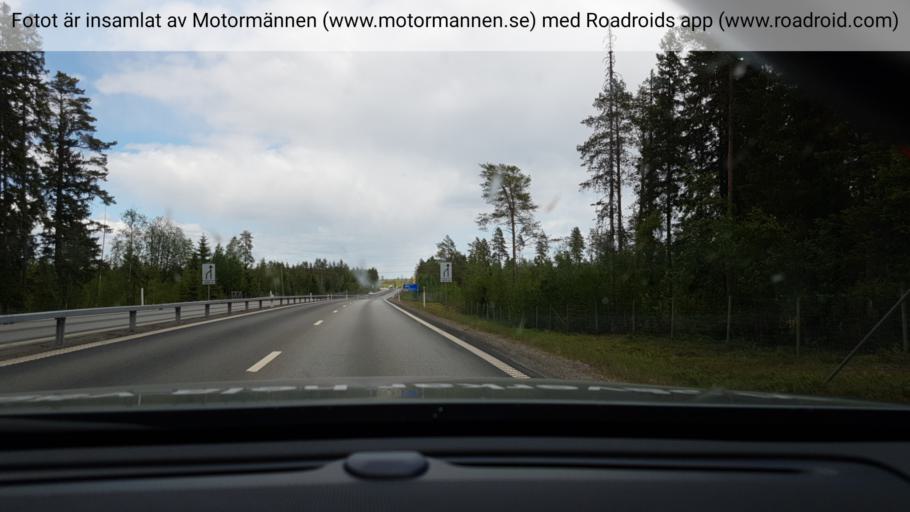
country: SE
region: Vaesterbotten
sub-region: Umea Kommun
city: Hoernefors
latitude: 63.6275
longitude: 19.8622
